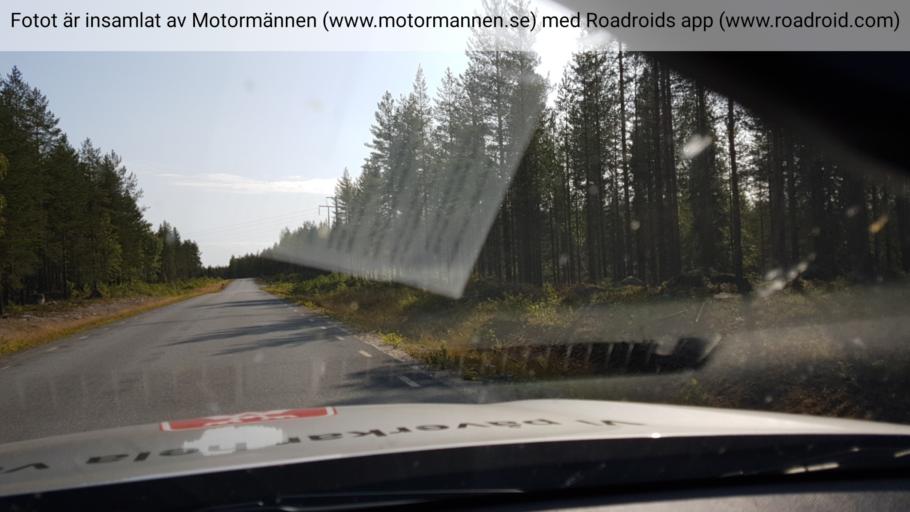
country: SE
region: Norrbotten
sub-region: Alvsbyns Kommun
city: AElvsbyn
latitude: 65.5925
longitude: 20.7254
